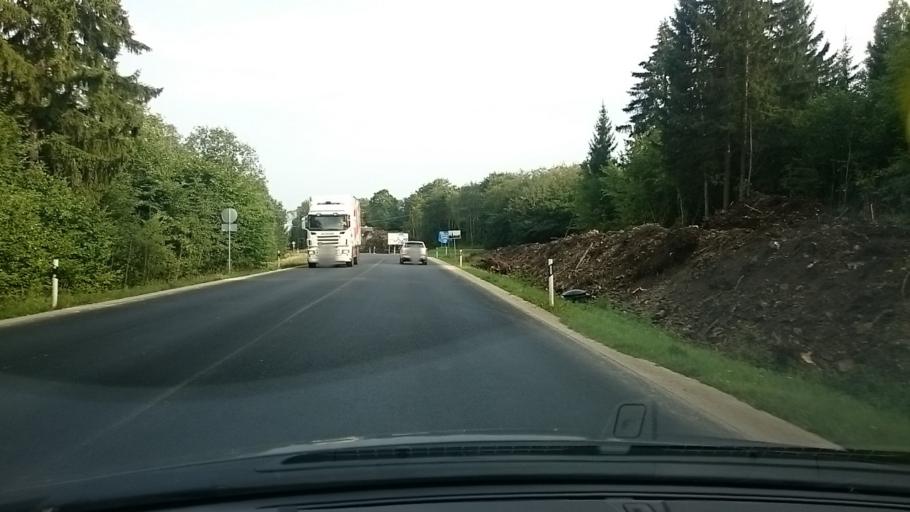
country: EE
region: Harju
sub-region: Saku vald
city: Saku
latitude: 59.3011
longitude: 24.6453
